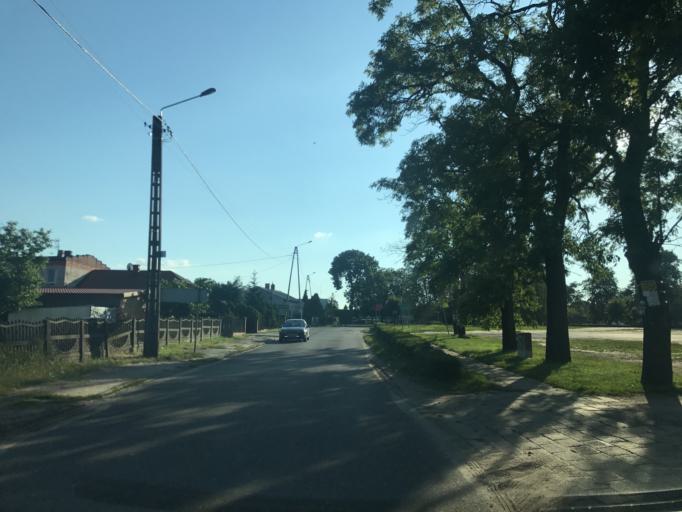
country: PL
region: Greater Poland Voivodeship
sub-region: Powiat turecki
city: Tuliszkow
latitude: 52.0760
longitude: 18.3033
